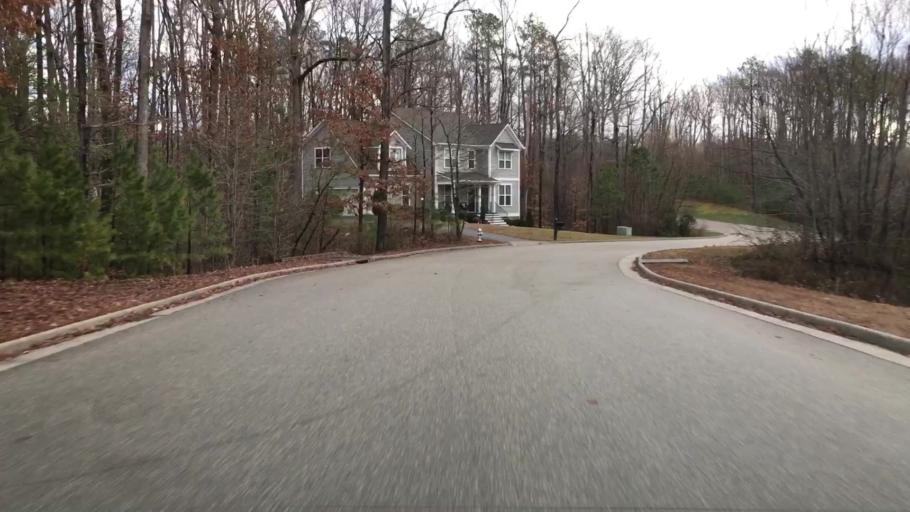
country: US
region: Virginia
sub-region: Chesterfield County
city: Bon Air
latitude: 37.4867
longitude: -77.6005
